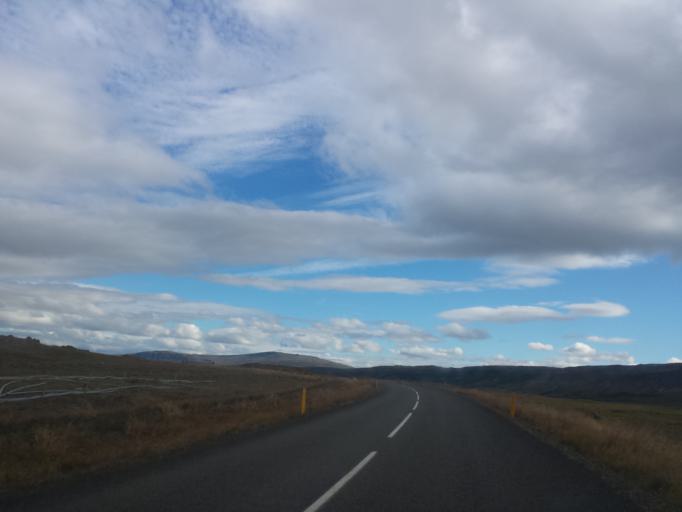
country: IS
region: West
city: Borgarnes
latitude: 64.4218
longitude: -21.7634
